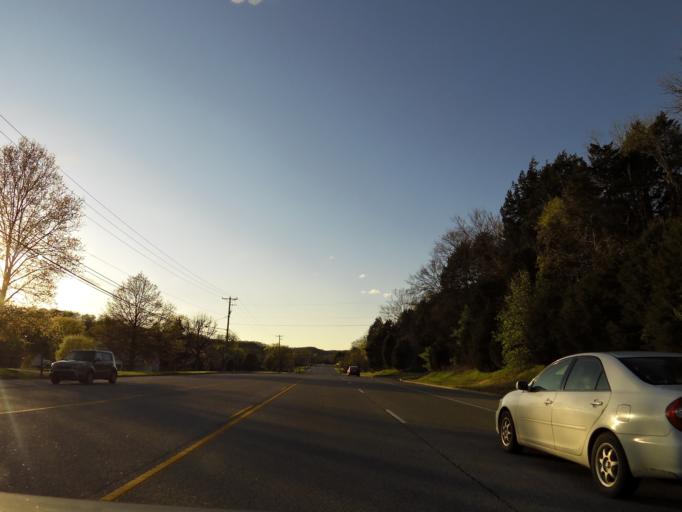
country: US
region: Tennessee
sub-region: Sumner County
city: Millersville
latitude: 36.3669
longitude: -86.7360
